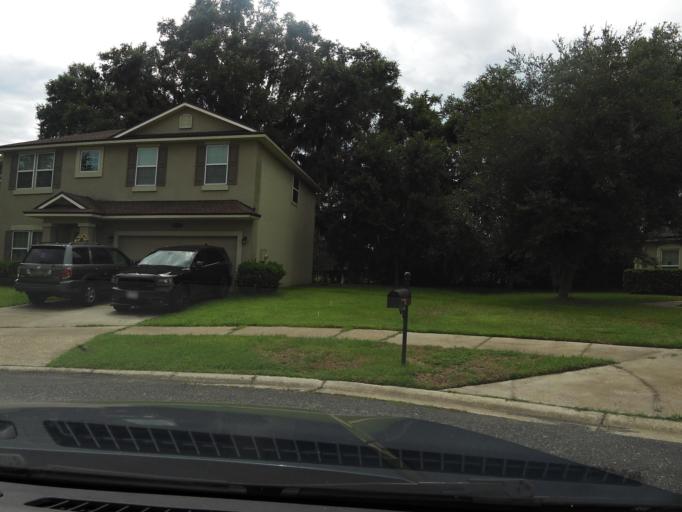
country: US
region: Florida
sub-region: Nassau County
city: Nassau Village-Ratliff
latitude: 30.4453
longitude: -81.7562
